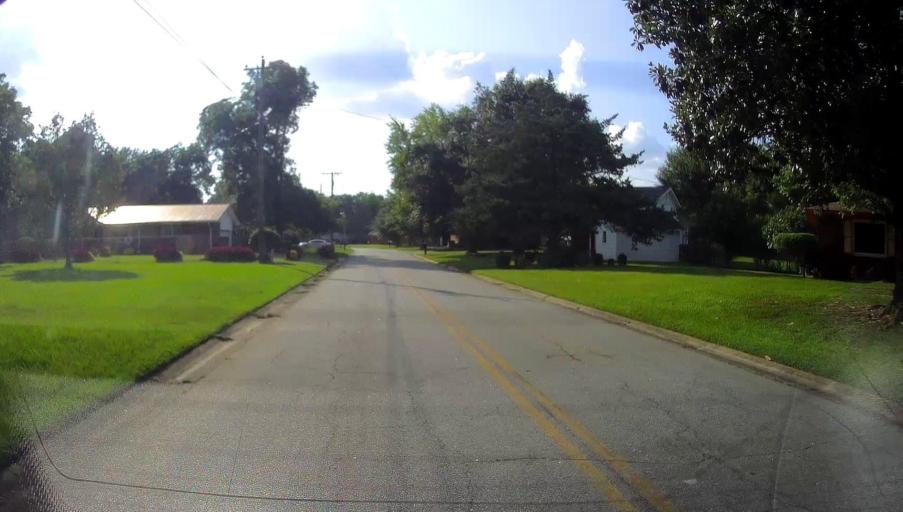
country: US
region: Georgia
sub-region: Houston County
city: Warner Robins
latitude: 32.5989
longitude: -83.6403
